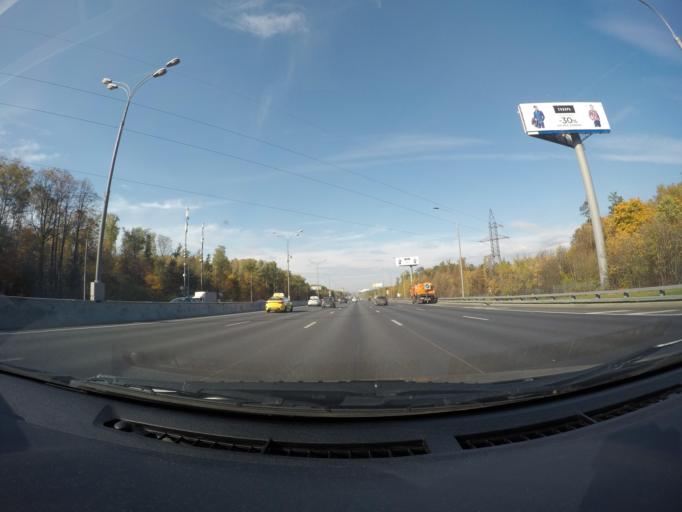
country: RU
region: Moskovskaya
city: Druzhba
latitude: 55.8604
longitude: 37.7691
